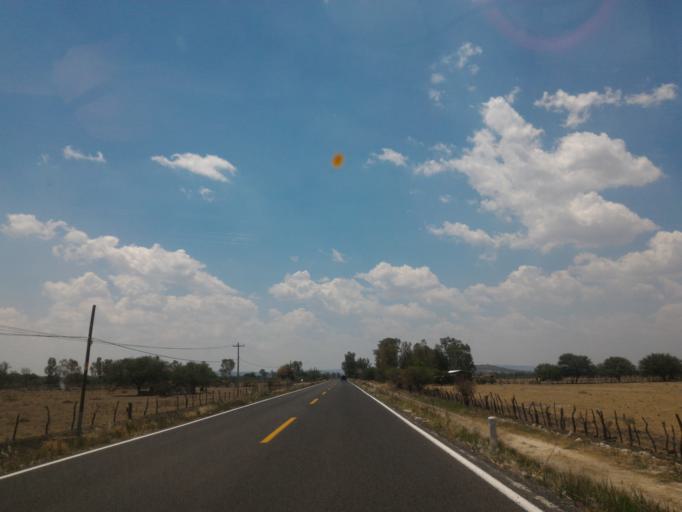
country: MX
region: Guanajuato
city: Ciudad Manuel Doblado
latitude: 20.7713
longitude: -101.9735
